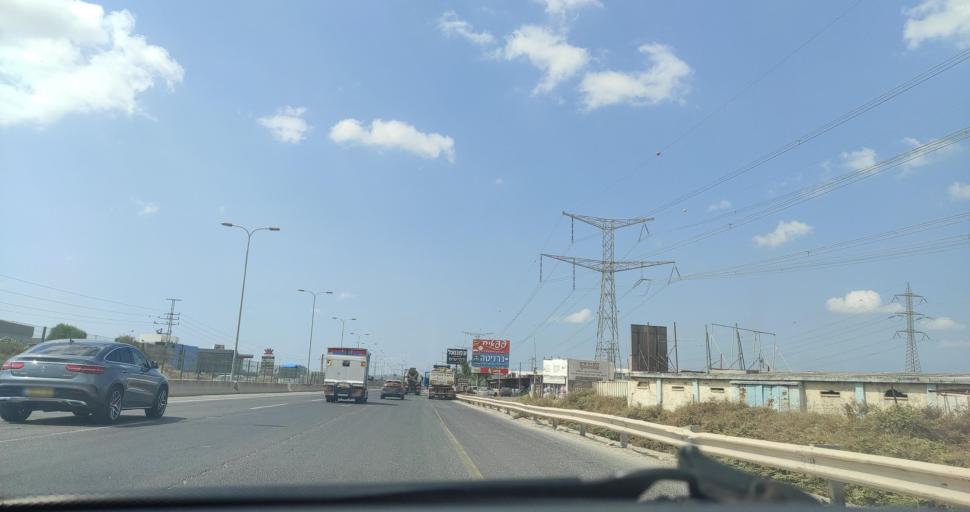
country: IL
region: Central District
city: Rosh Ha'Ayin
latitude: 32.1125
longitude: 34.9532
